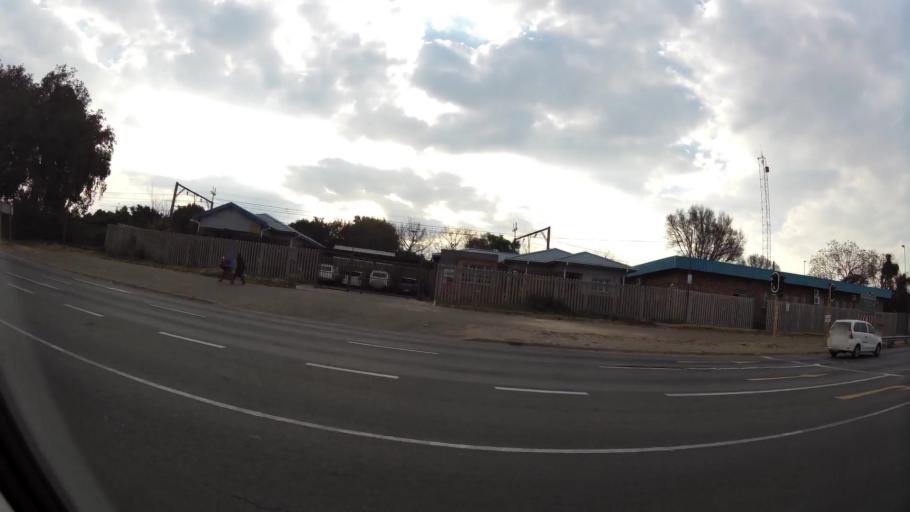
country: ZA
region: Gauteng
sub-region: Ekurhuleni Metropolitan Municipality
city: Germiston
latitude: -26.2421
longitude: 28.1936
